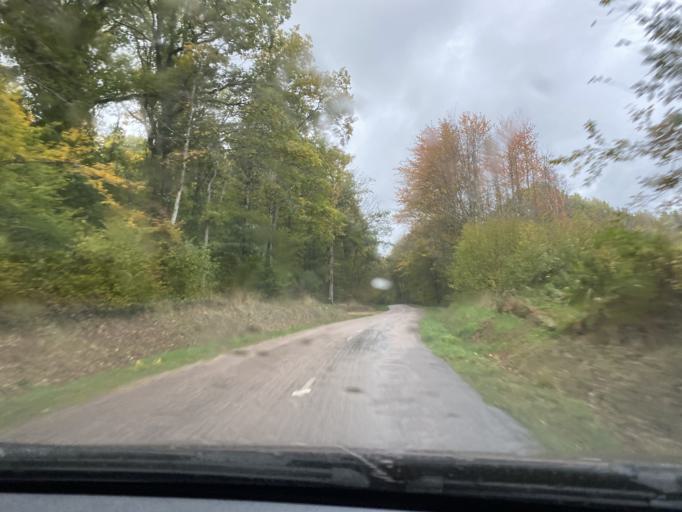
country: FR
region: Bourgogne
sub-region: Departement de la Cote-d'Or
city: Saulieu
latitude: 47.3507
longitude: 4.2397
